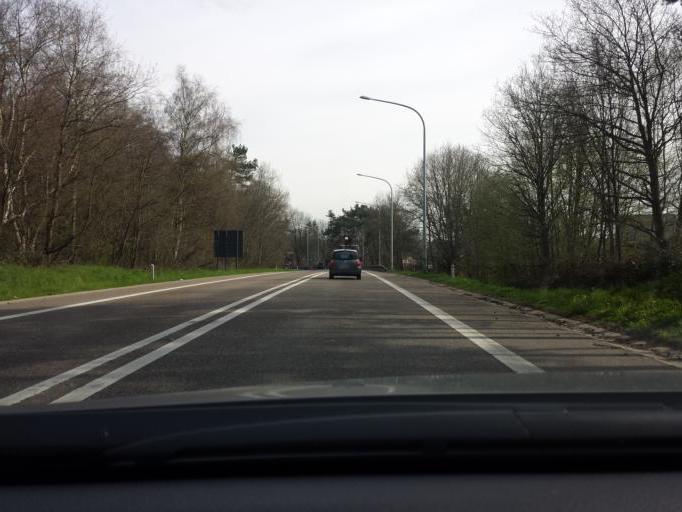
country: BE
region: Flanders
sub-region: Provincie Limburg
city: Beringen
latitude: 51.0404
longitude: 5.1856
